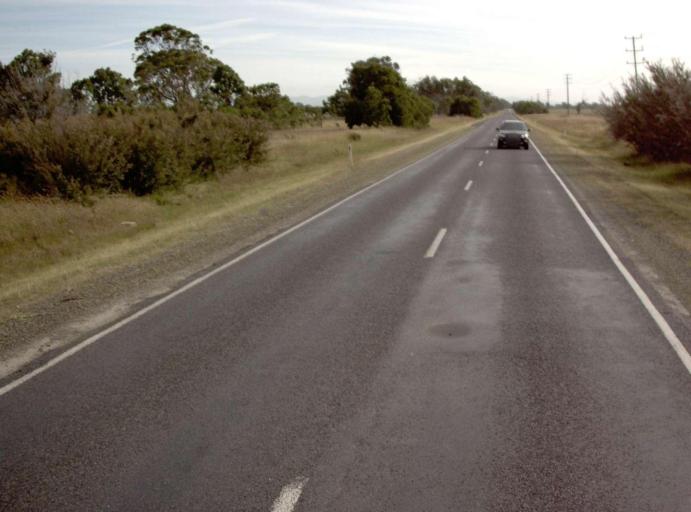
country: AU
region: Victoria
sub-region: Latrobe
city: Traralgon
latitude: -38.0822
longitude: 146.6070
